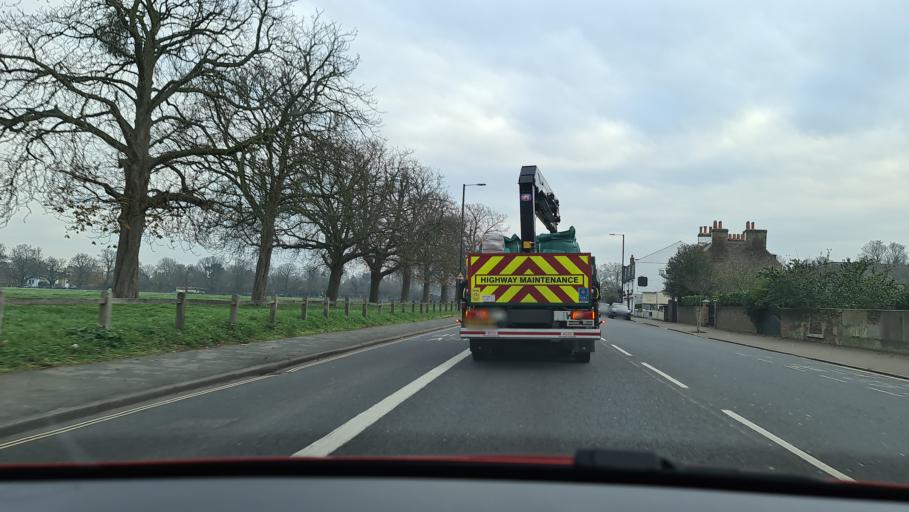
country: GB
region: England
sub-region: Surrey
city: East Molesey
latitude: 51.4071
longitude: -0.3452
